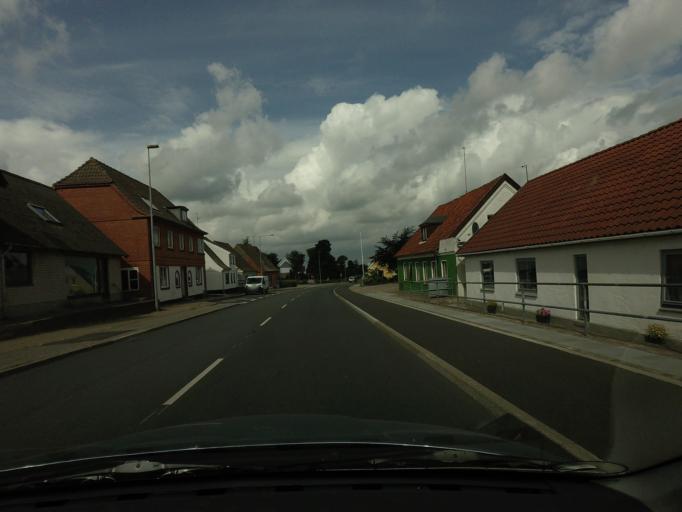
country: DK
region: North Denmark
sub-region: Hjorring Kommune
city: Tars
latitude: 57.3838
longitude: 10.1194
